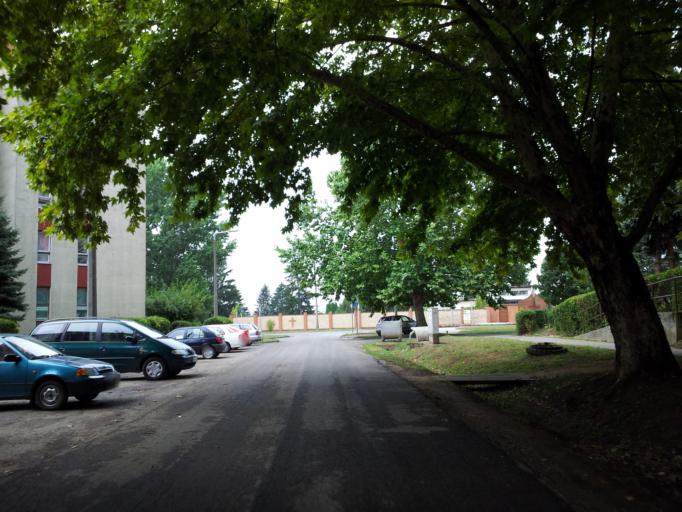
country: HU
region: Tolna
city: Tamasi
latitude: 46.6388
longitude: 18.2810
